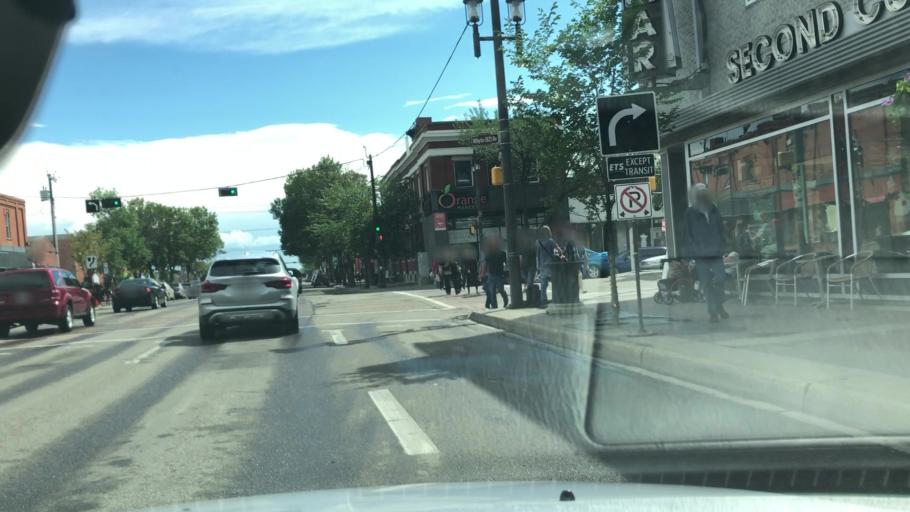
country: CA
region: Alberta
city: Edmonton
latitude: 53.5185
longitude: -113.4976
